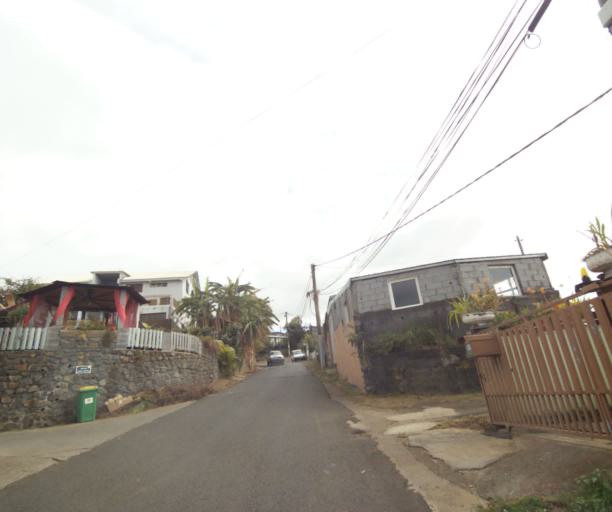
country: RE
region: Reunion
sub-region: Reunion
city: Saint-Paul
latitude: -21.0281
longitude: 55.3084
